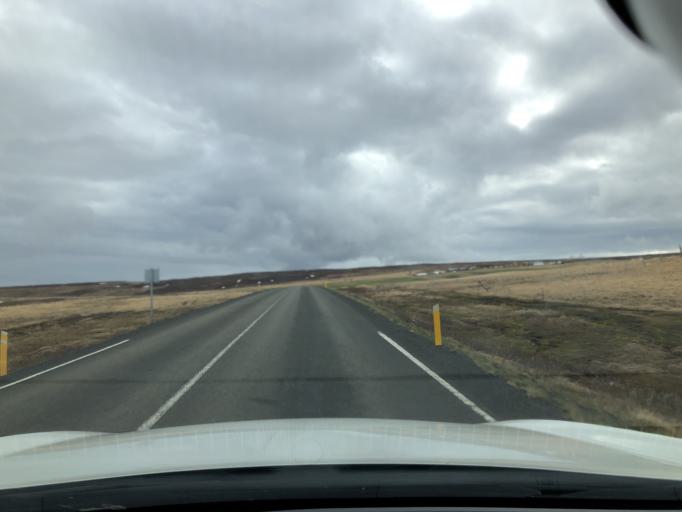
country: IS
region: Northeast
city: Laugar
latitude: 65.6865
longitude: -17.5344
